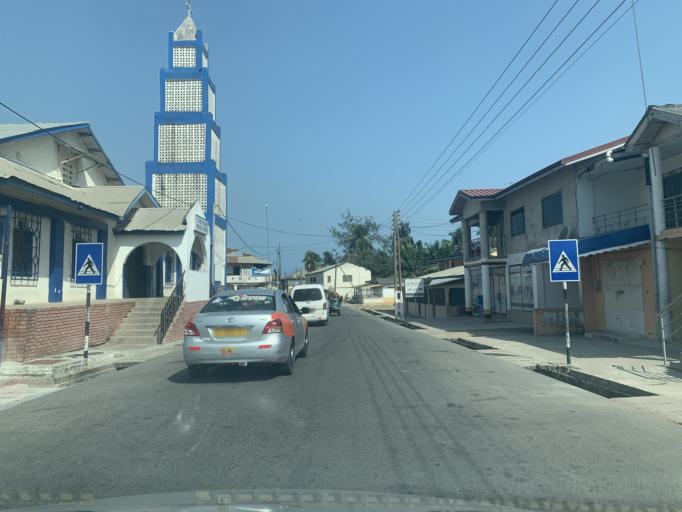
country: GH
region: Central
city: Winneba
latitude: 5.3435
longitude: -0.6272
